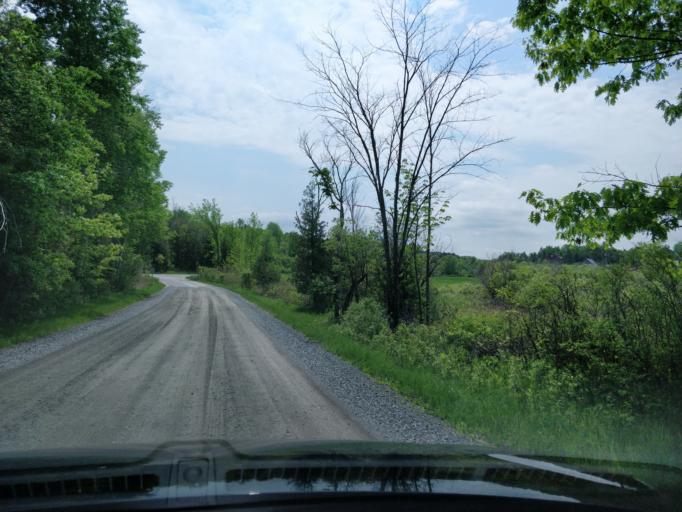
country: CA
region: Ontario
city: Perth
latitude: 44.6586
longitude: -76.5782
